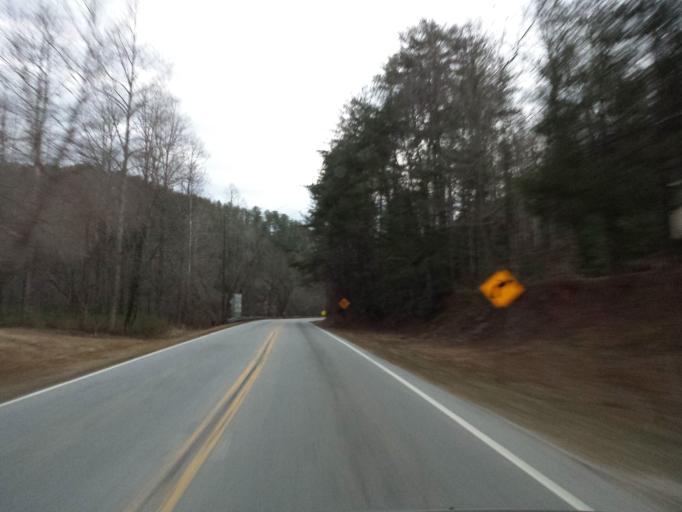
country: US
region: Georgia
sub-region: White County
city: Cleveland
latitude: 34.6915
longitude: -83.7135
